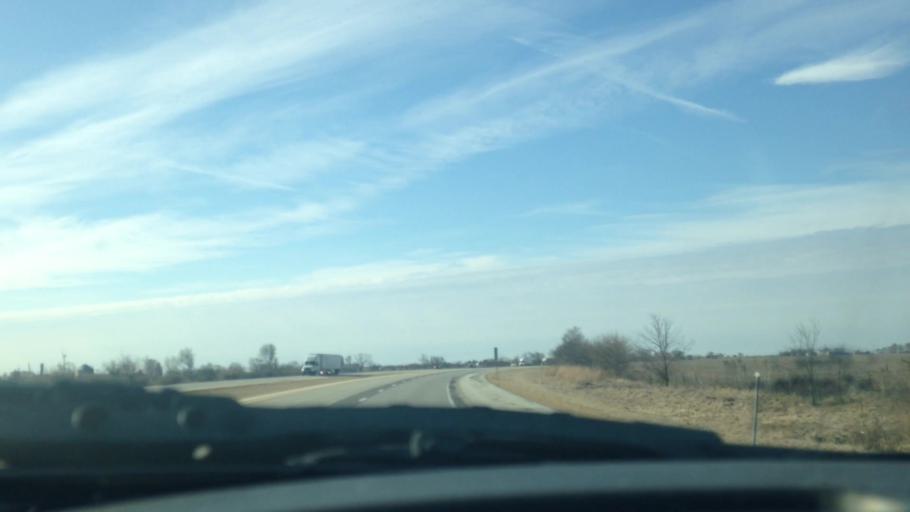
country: US
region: Illinois
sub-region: Ford County
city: Paxton
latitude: 40.5090
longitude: -88.0848
